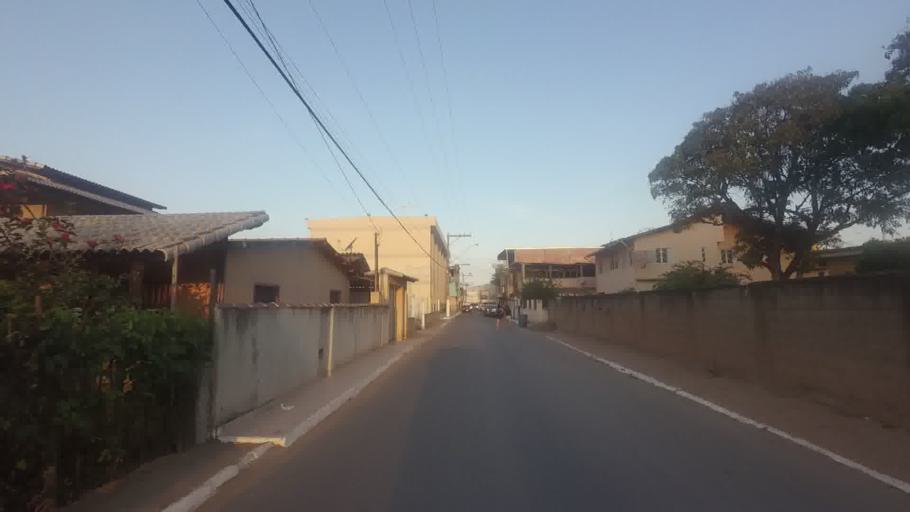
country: BR
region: Espirito Santo
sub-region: Piuma
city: Piuma
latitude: -20.8882
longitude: -40.7757
